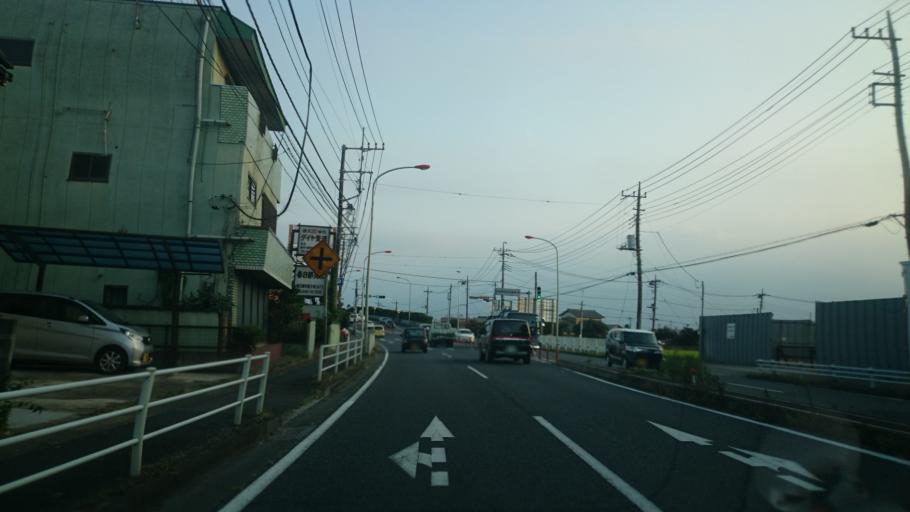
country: JP
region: Saitama
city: Kasukabe
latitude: 35.9766
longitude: 139.7360
